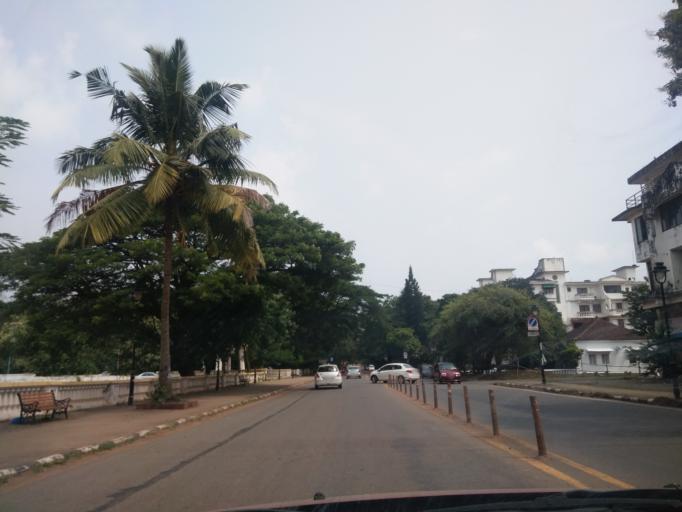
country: IN
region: Goa
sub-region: North Goa
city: Panaji
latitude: 15.4922
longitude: 73.8171
